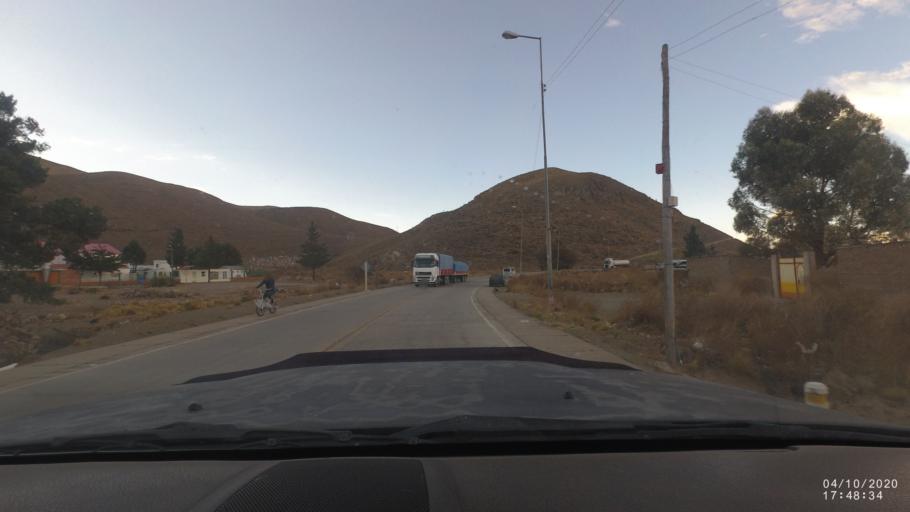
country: BO
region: Oruro
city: Oruro
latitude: -18.0162
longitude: -67.1395
